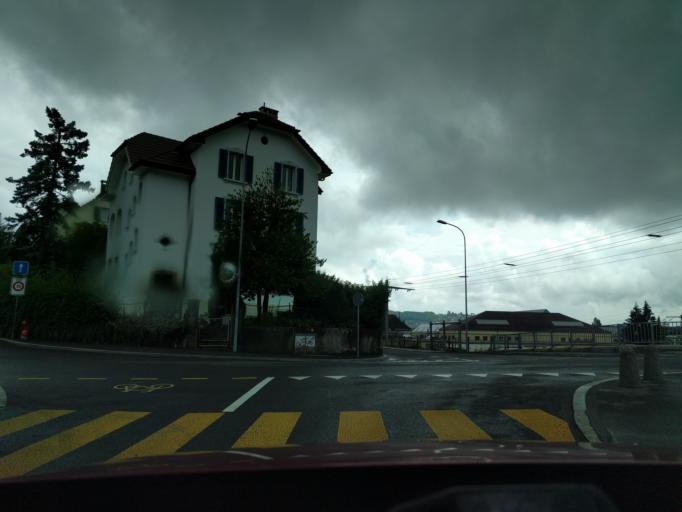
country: CH
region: Bern
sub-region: Biel/Bienne District
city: Biel/Bienne
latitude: 47.1329
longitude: 7.2585
